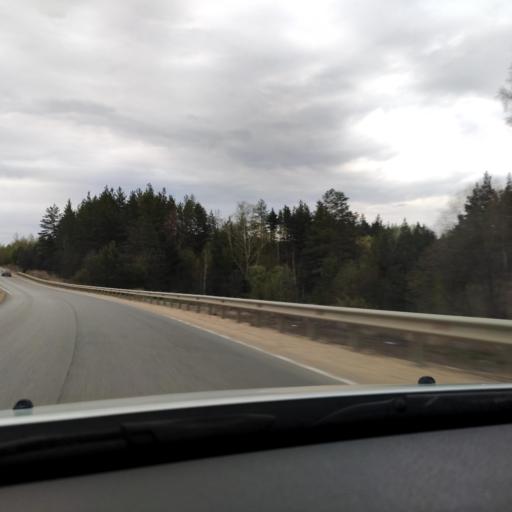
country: RU
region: Lipetsk
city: Zadonsk
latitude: 52.4238
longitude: 38.9503
